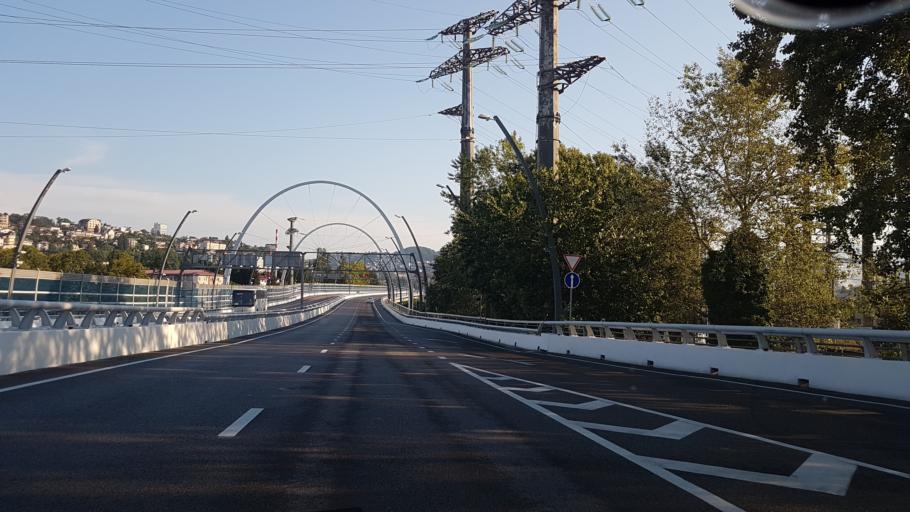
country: RU
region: Krasnodarskiy
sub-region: Sochi City
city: Sochi
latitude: 43.5988
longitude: 39.7307
